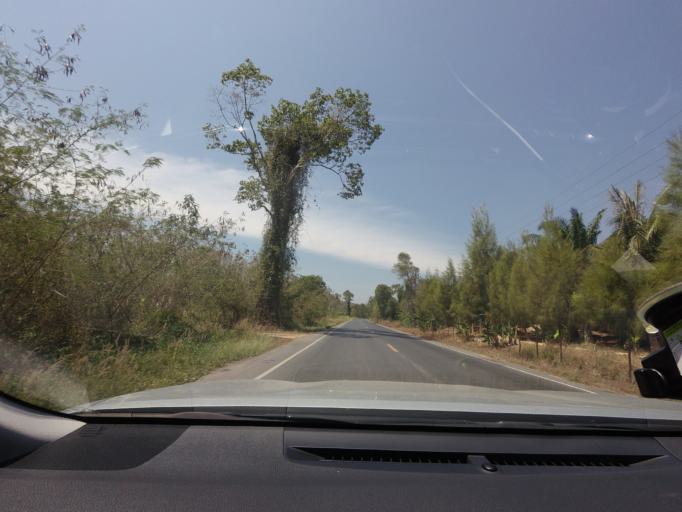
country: TH
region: Surat Thani
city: Tha Chang
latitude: 9.2620
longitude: 99.1761
